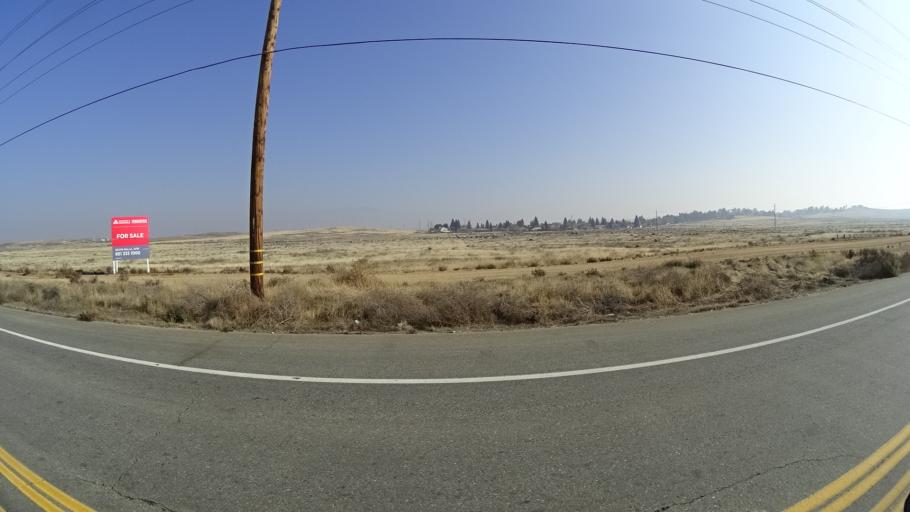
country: US
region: California
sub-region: Kern County
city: Oildale
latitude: 35.4098
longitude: -118.8802
